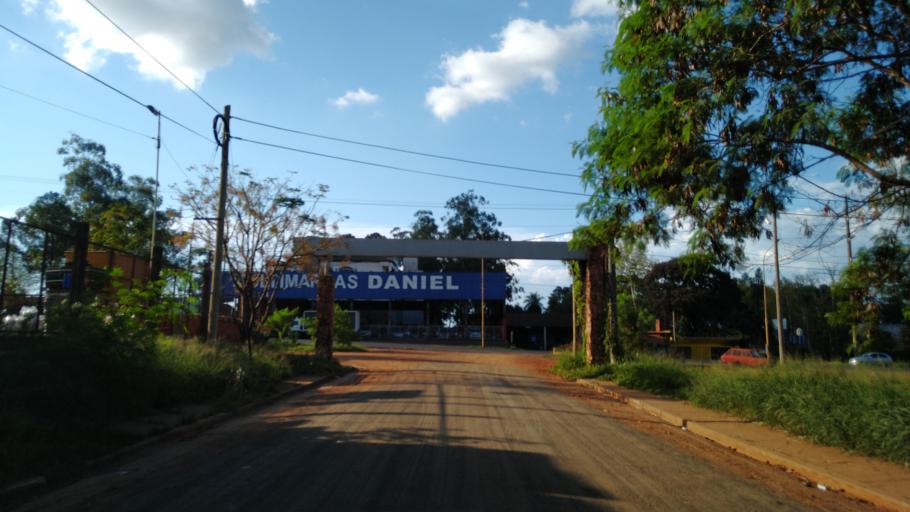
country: AR
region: Misiones
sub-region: Departamento de Capital
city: Posadas
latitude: -27.4033
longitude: -55.9198
